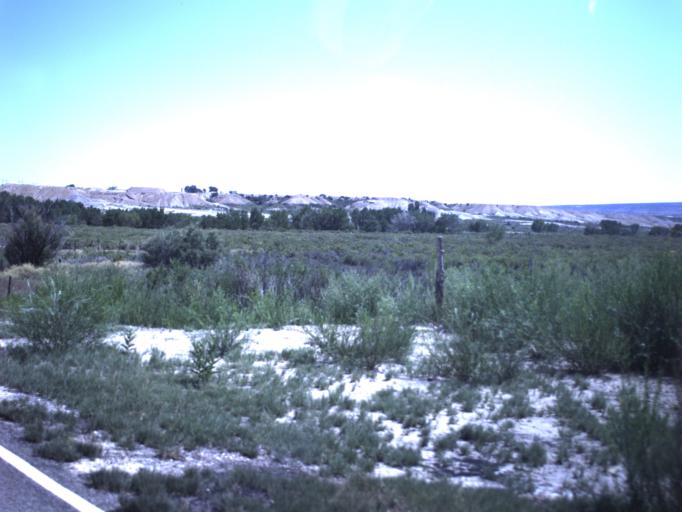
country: US
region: Utah
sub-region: Emery County
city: Ferron
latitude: 38.8726
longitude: -111.2934
